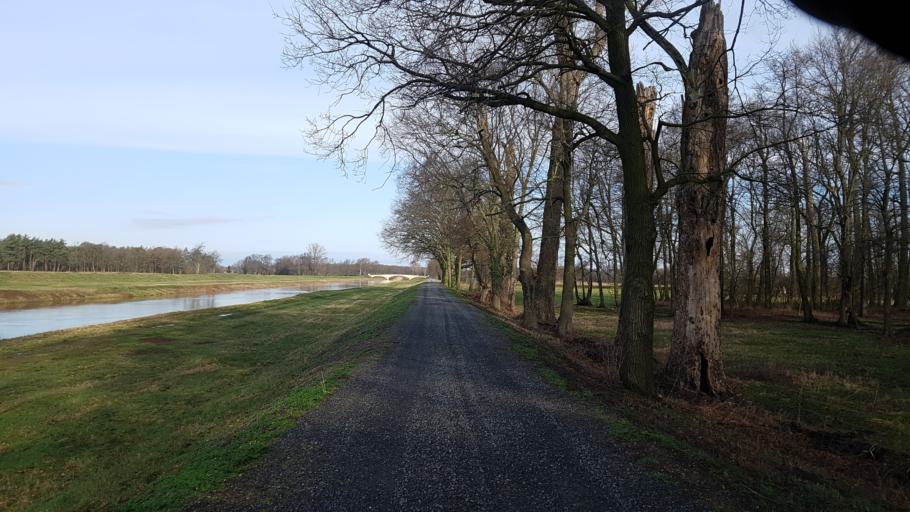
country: DE
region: Brandenburg
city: Falkenberg
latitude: 51.6292
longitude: 13.2824
